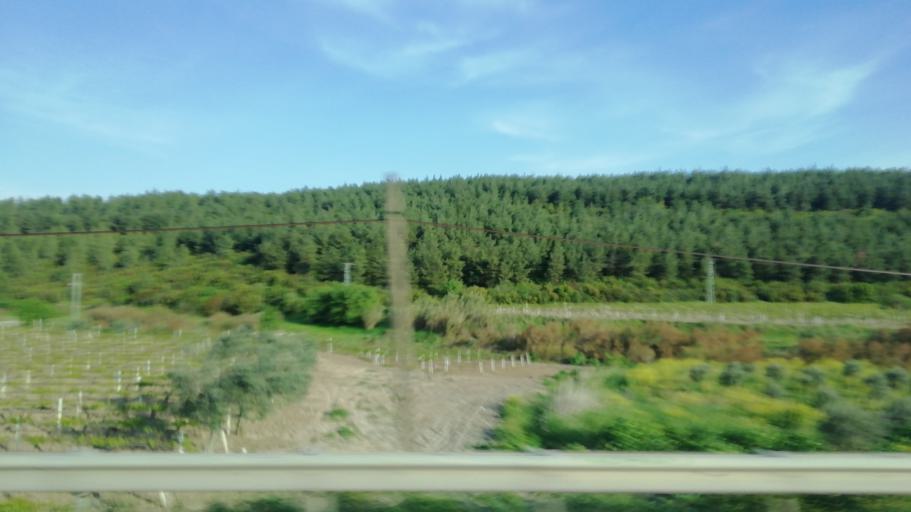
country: TR
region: Manisa
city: Halitpasa
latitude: 38.7910
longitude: 27.6793
